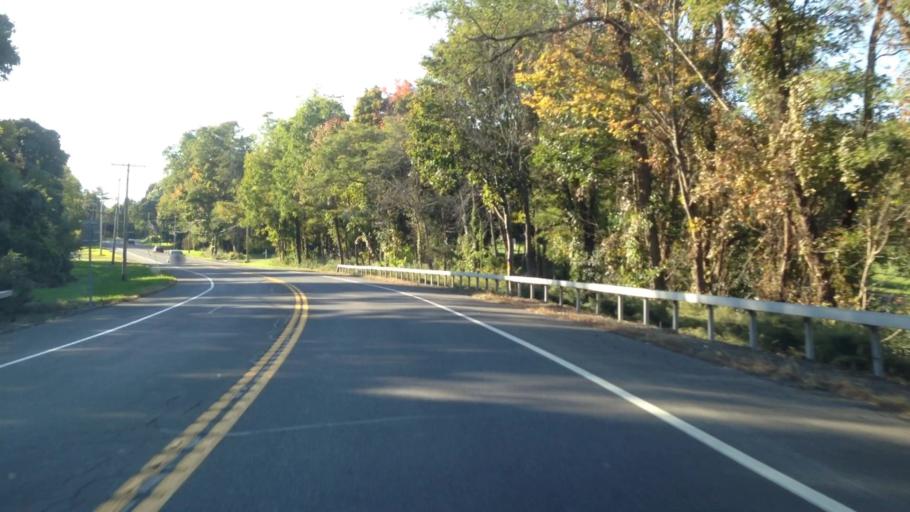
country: US
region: New York
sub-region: Dutchess County
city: Hyde Park
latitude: 41.7914
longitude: -73.9605
